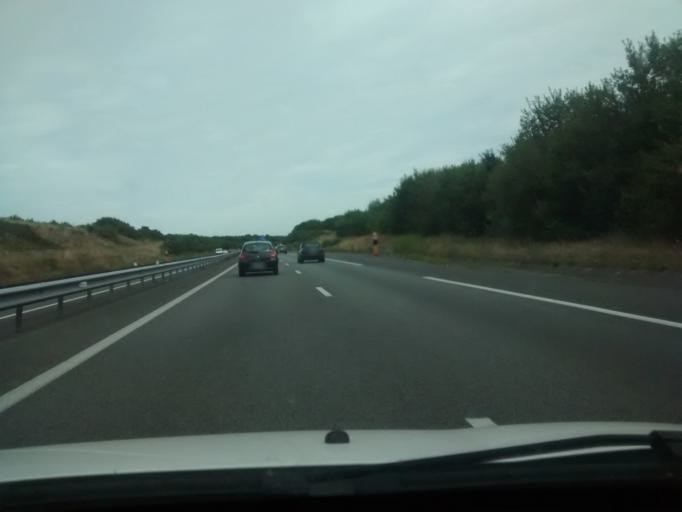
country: FR
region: Brittany
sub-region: Departement d'Ille-et-Vilaine
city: Saint-Aubin-du-Cormier
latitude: 48.2544
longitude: -1.4230
